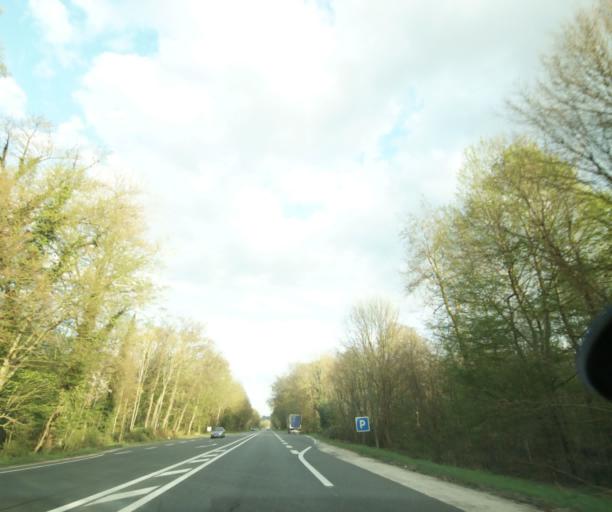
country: FR
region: Ile-de-France
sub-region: Departement de Seine-et-Marne
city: Barbizon
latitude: 48.4501
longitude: 2.6270
